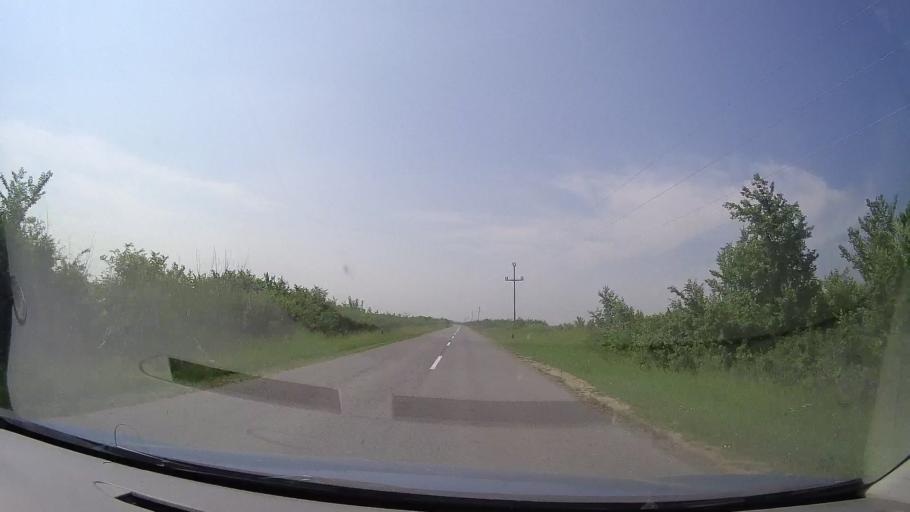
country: RS
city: Jarkovac
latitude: 45.2608
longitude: 20.7639
